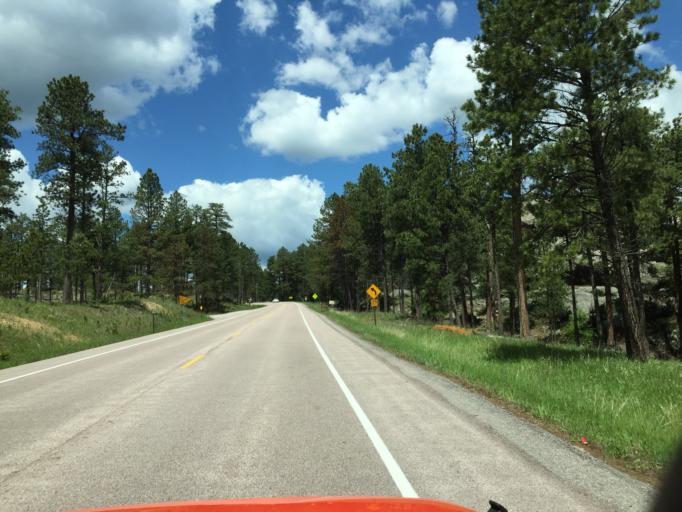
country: US
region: South Dakota
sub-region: Custer County
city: Custer
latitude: 43.8969
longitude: -103.4827
